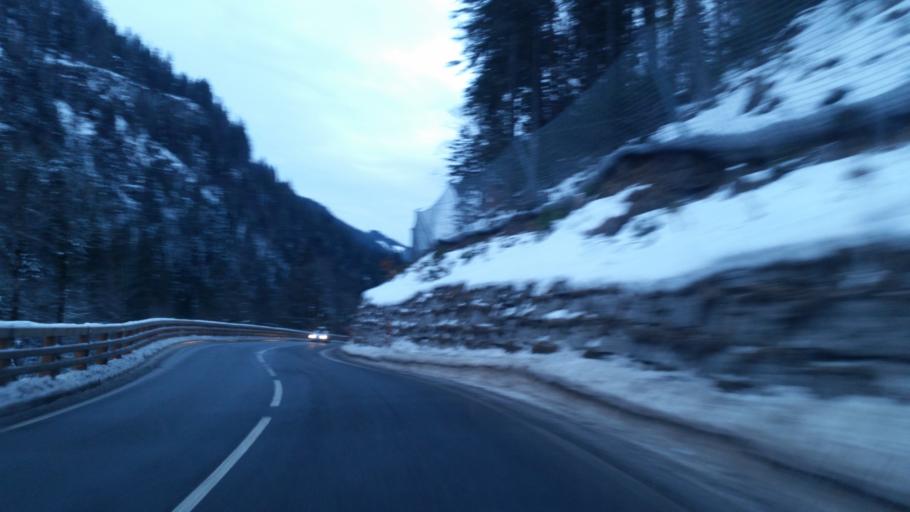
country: AT
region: Salzburg
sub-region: Politischer Bezirk Sankt Johann im Pongau
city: Untertauern
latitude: 47.2863
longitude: 13.5064
